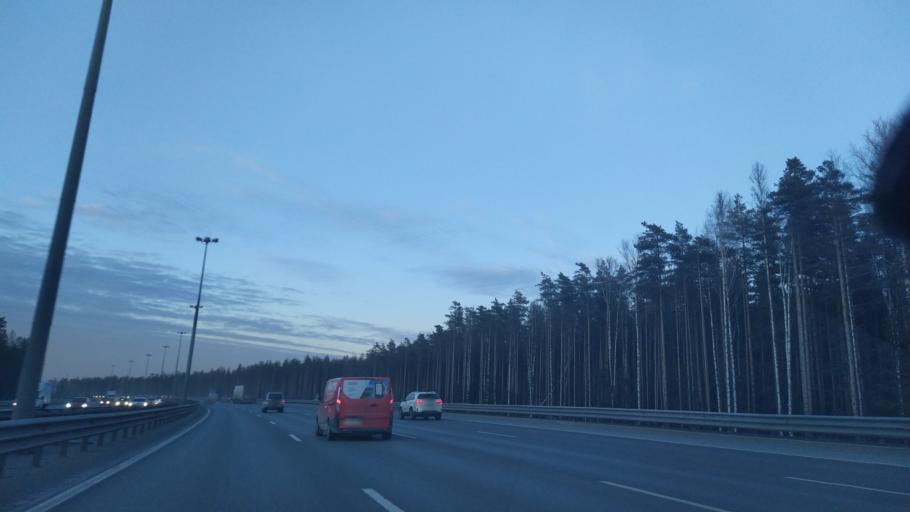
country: RU
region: Leningrad
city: Yanino Vtoroye
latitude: 59.9598
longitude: 30.5538
